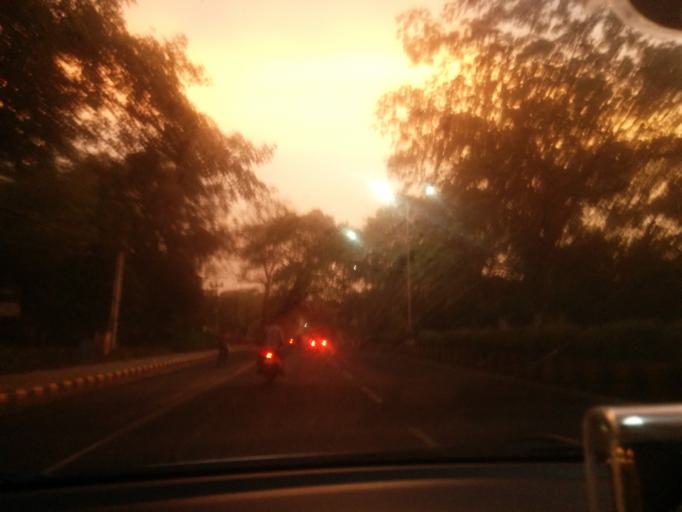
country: IN
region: Andhra Pradesh
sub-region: East Godavari
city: Rajahmundry
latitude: 17.0165
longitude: 81.7884
